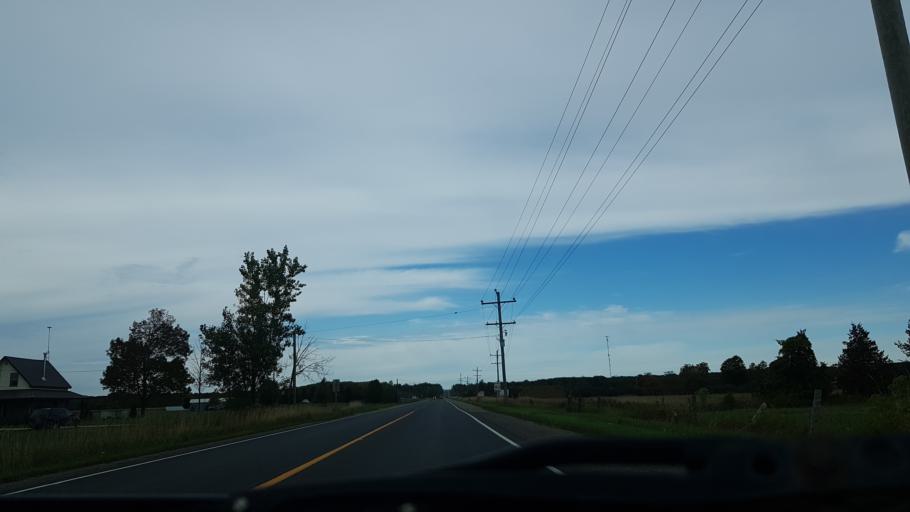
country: CA
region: Ontario
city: Angus
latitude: 44.3144
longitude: -80.0732
